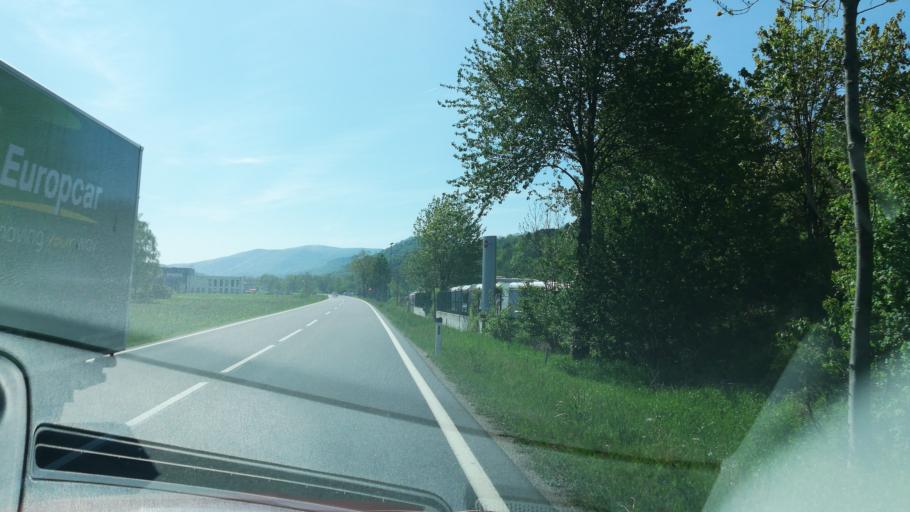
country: AT
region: Lower Austria
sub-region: Politischer Bezirk Baden
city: Alland
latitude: 48.0661
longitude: 16.0652
